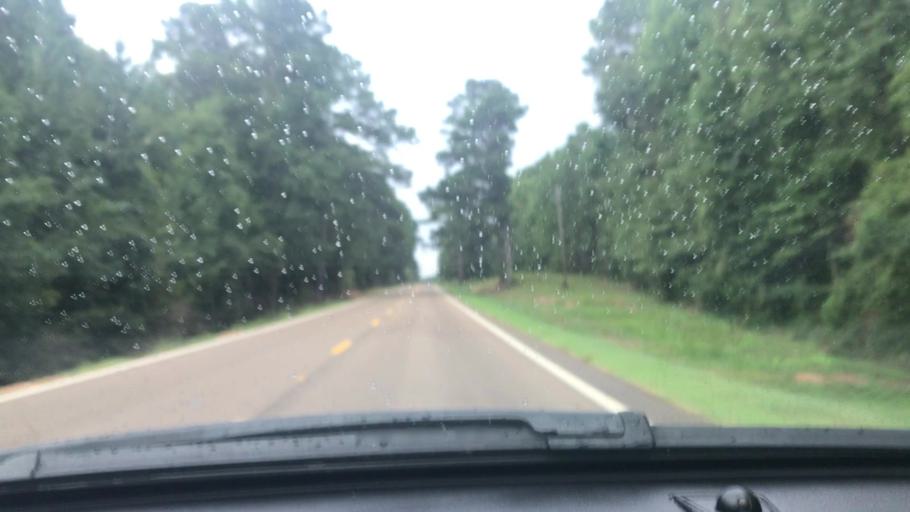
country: US
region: Mississippi
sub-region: Pike County
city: Summit
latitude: 31.3490
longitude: -90.5985
